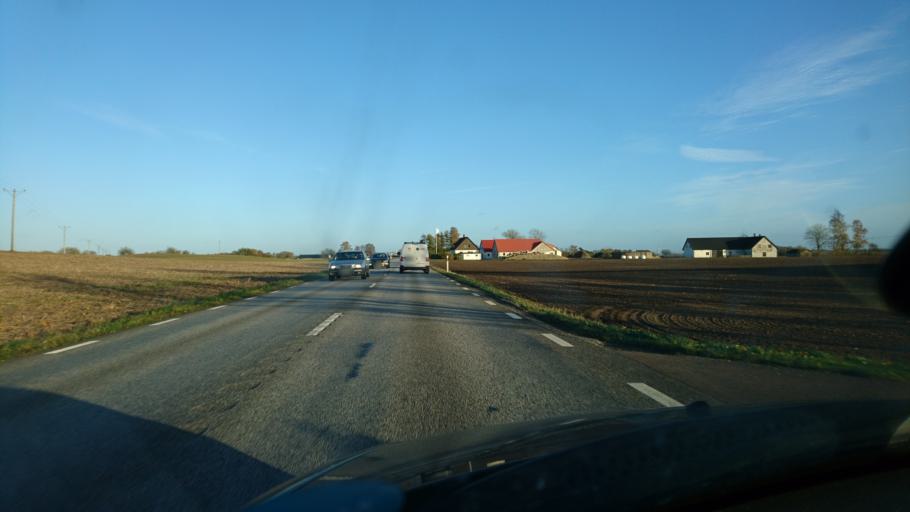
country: SE
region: Skane
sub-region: Tomelilla Kommun
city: Tomelilla
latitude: 55.5455
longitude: 14.0217
